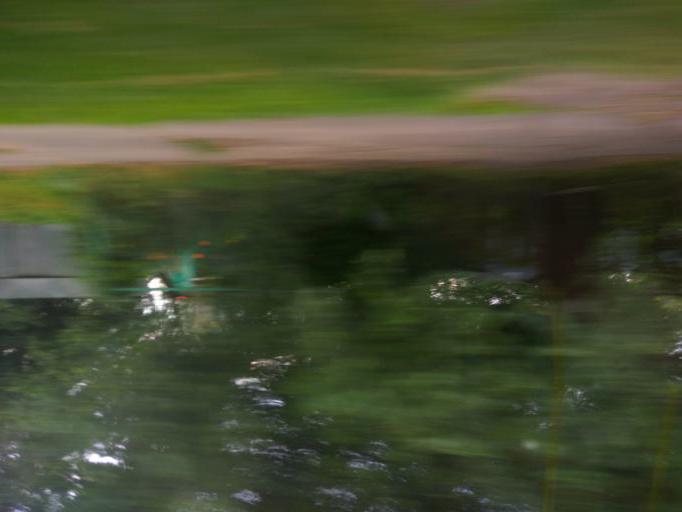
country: RU
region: Moscow
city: Annino
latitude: 55.5962
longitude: 37.6194
